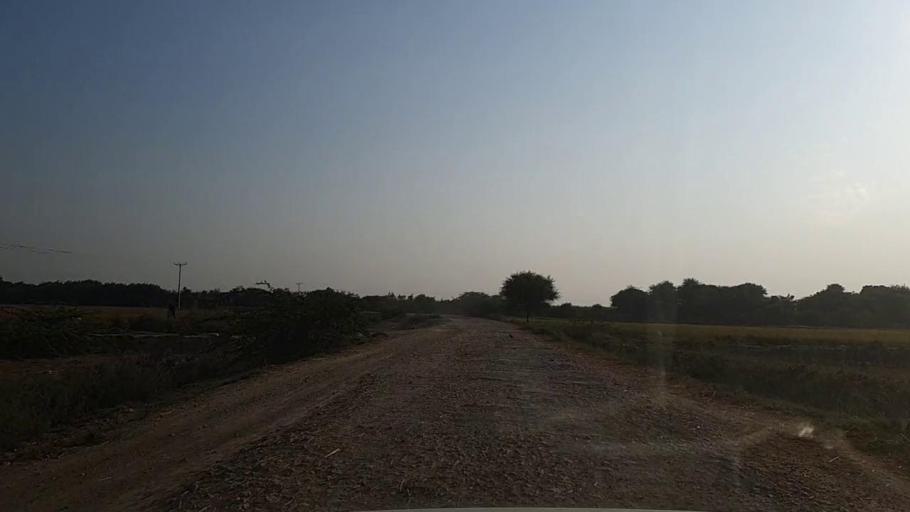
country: PK
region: Sindh
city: Mirpur Batoro
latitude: 24.7577
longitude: 68.2310
